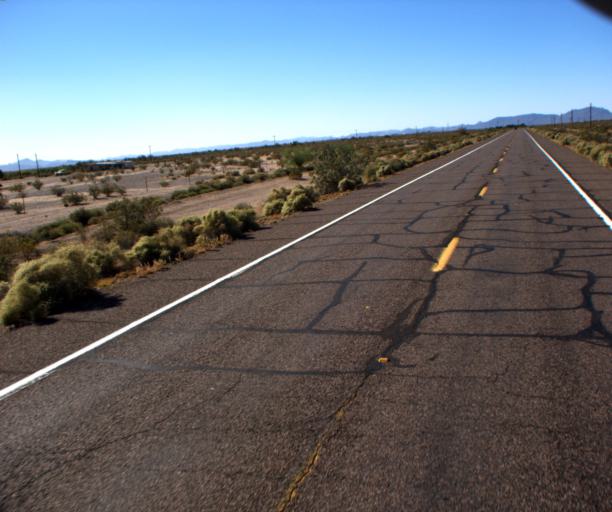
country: US
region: Arizona
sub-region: Maricopa County
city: Gila Bend
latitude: 32.9220
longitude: -112.7347
